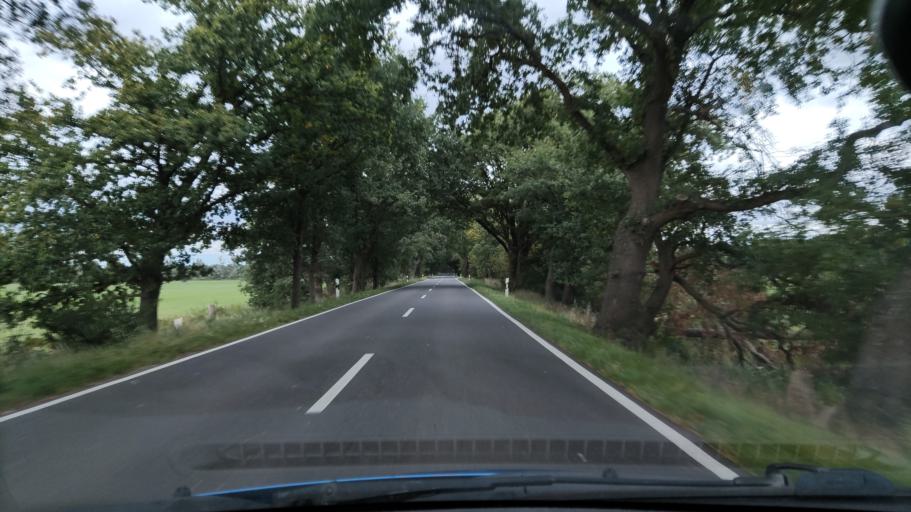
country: DE
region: Lower Saxony
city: Neu Darchau
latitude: 53.3436
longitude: 10.9543
